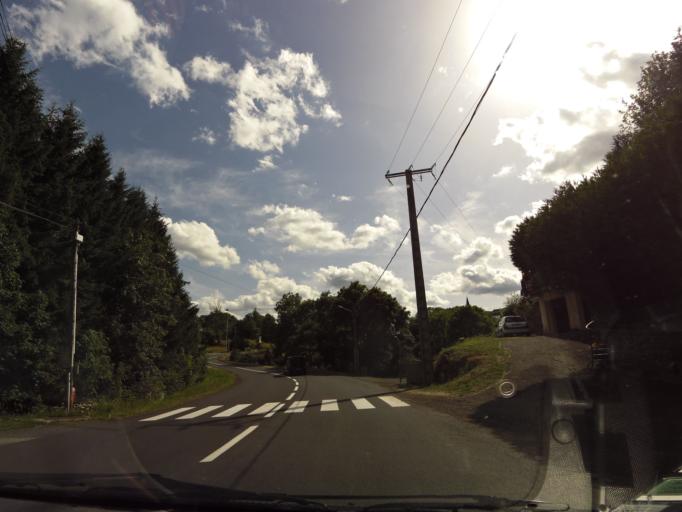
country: FR
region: Auvergne
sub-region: Departement du Puy-de-Dome
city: Mont-Dore
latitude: 45.5163
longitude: 2.9388
